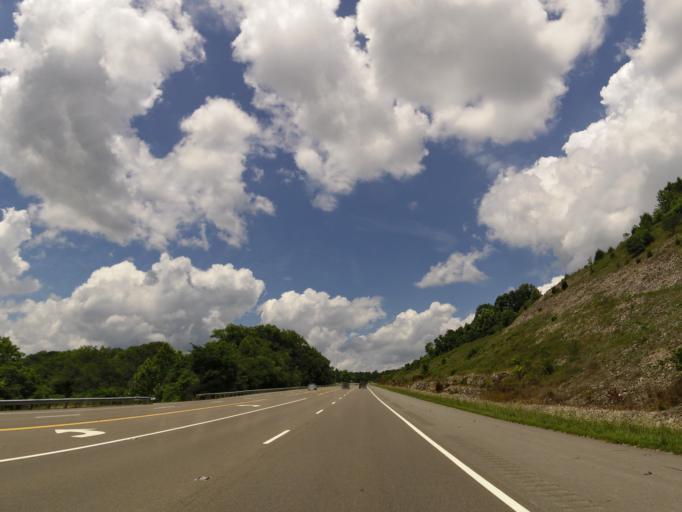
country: US
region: Tennessee
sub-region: Claiborne County
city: New Tazewell
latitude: 36.5176
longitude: -83.6126
